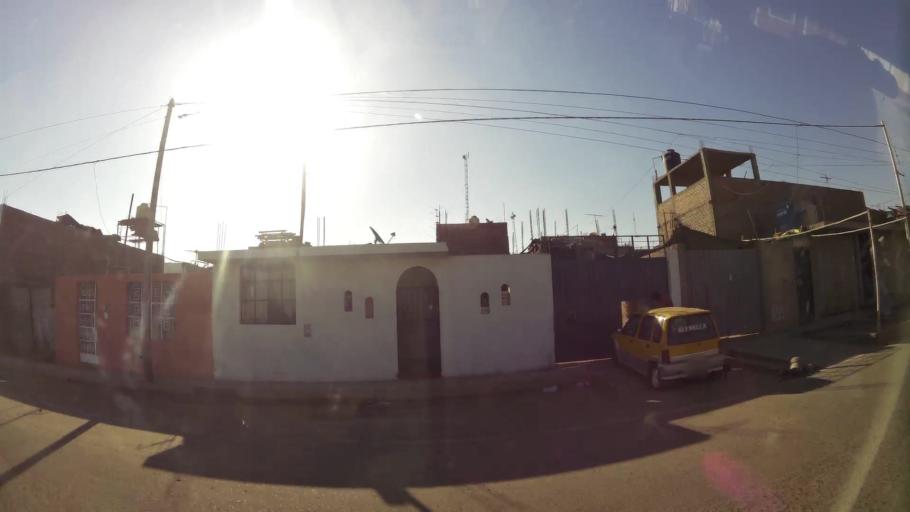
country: PE
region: Ica
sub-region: Provincia de Ica
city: La Tinguina
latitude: -14.0504
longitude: -75.6959
